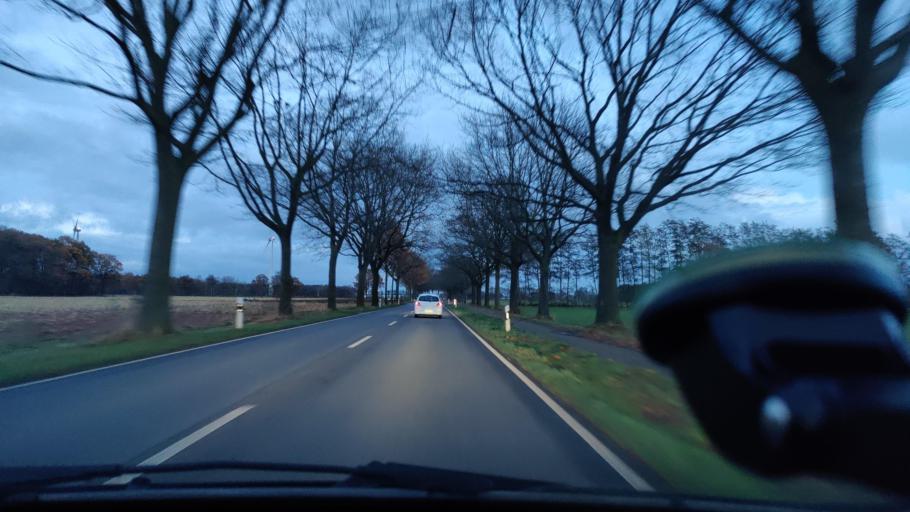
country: DE
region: North Rhine-Westphalia
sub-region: Regierungsbezirk Dusseldorf
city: Weeze
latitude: 51.5740
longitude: 6.1895
